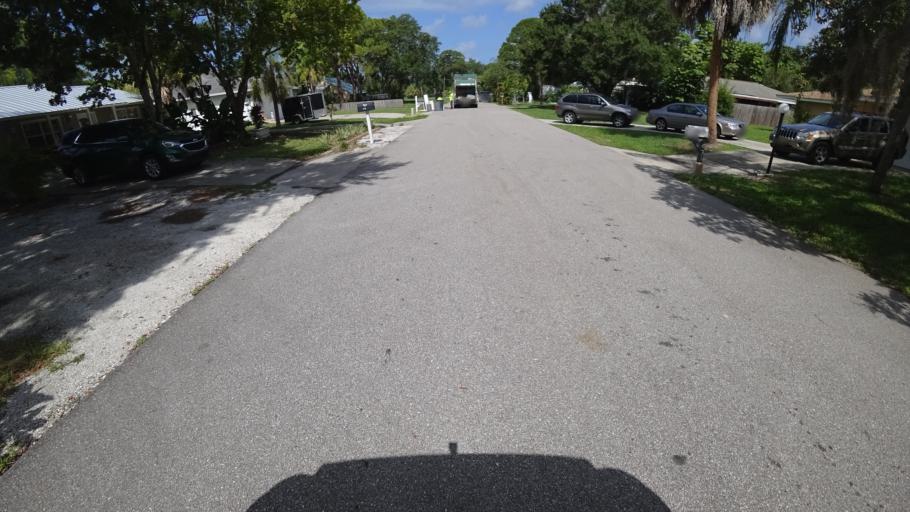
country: US
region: Florida
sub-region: Manatee County
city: Whitfield
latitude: 27.3933
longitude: -82.5651
